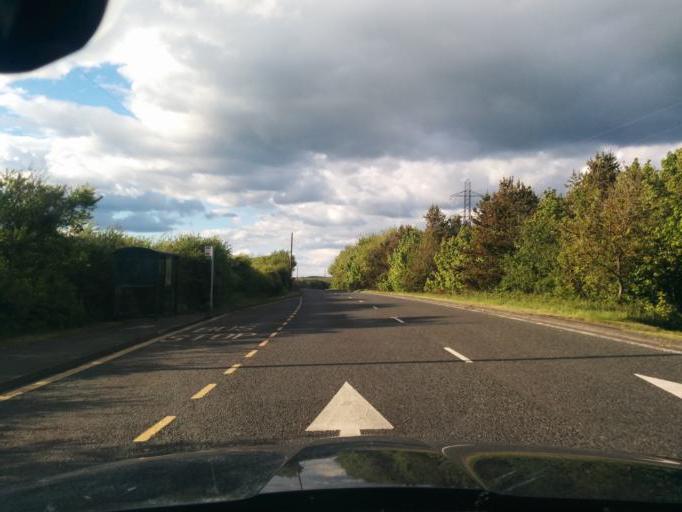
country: GB
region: England
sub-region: Northumberland
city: Cramlington
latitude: 55.0900
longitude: -1.6201
